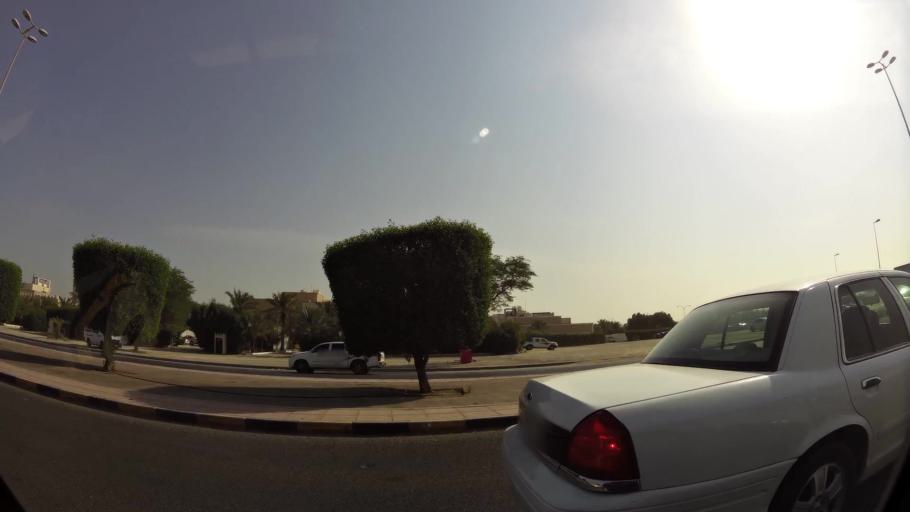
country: KW
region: Al Ahmadi
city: Ar Riqqah
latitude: 29.1582
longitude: 48.0948
